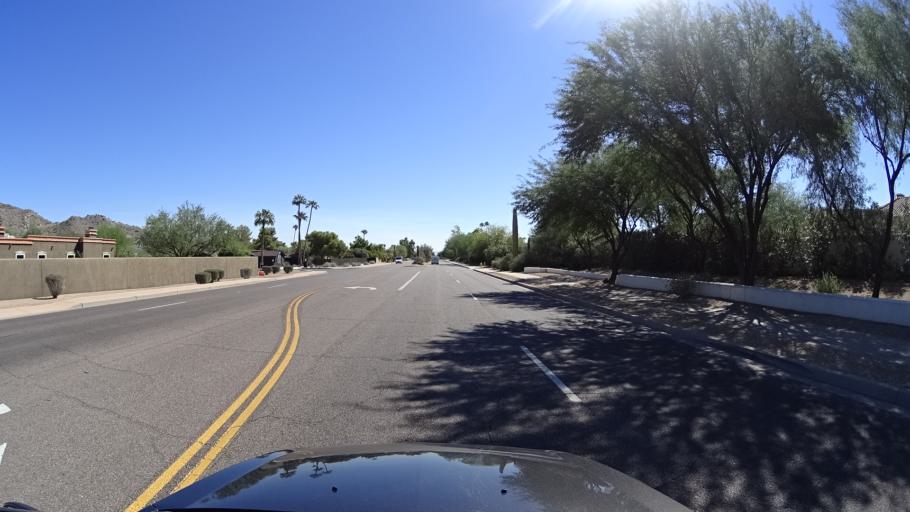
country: US
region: Arizona
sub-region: Maricopa County
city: Paradise Valley
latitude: 33.5310
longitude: -111.9526
